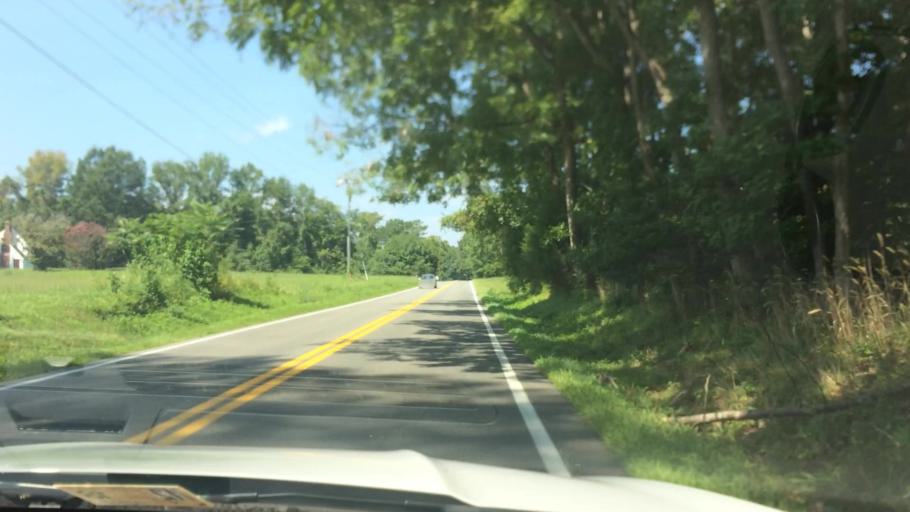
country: US
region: Virginia
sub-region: New Kent County
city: New Kent
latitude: 37.5237
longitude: -77.0591
